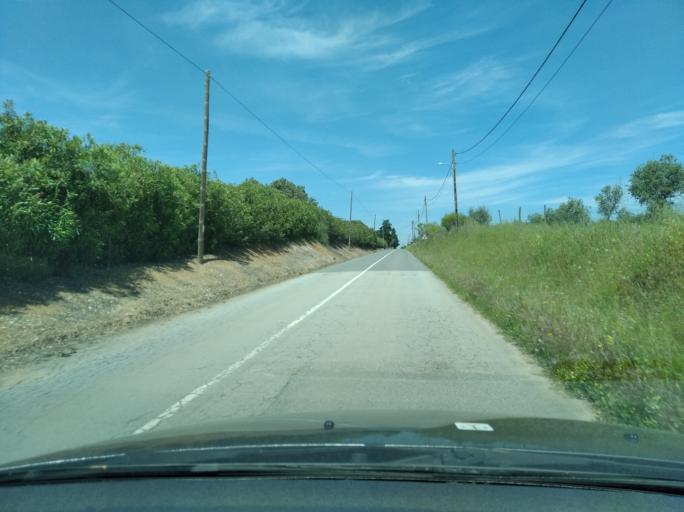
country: PT
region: Portalegre
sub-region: Avis
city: Avis
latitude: 39.0861
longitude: -7.8792
